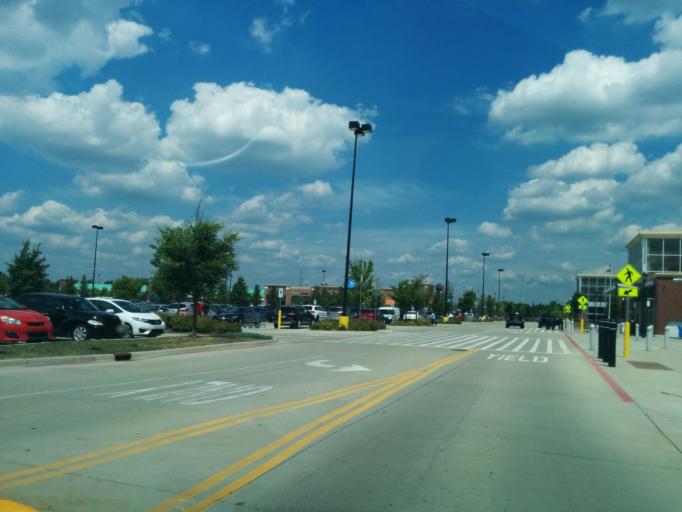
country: US
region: Michigan
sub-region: Oakland County
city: Novi
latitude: 42.4812
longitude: -83.4715
